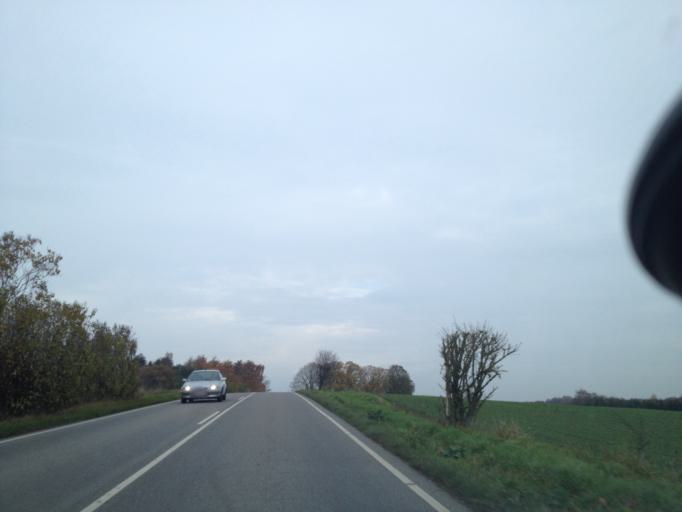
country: DK
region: South Denmark
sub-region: Nordfyns Kommune
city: Bogense
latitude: 55.5110
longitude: 10.0990
